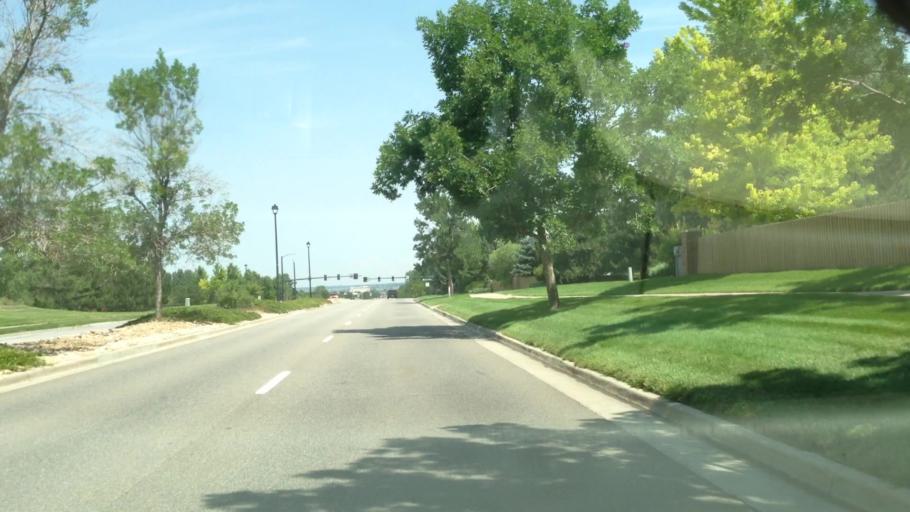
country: US
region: Colorado
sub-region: Douglas County
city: Stonegate
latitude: 39.5218
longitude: -104.7934
